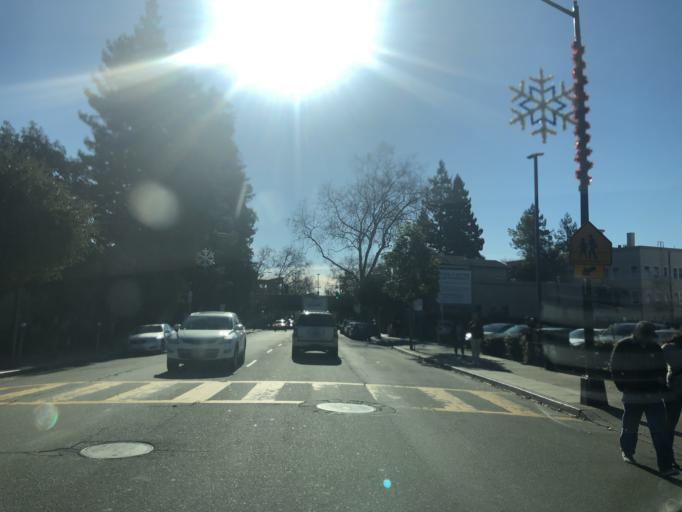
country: US
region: California
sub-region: Alameda County
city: Piedmont
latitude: 37.8460
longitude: -122.2520
